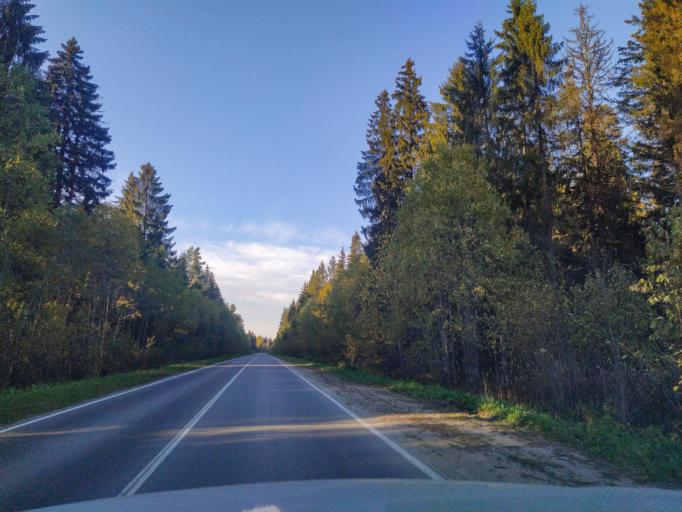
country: RU
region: Leningrad
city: Siverskiy
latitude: 59.3036
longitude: 30.0347
